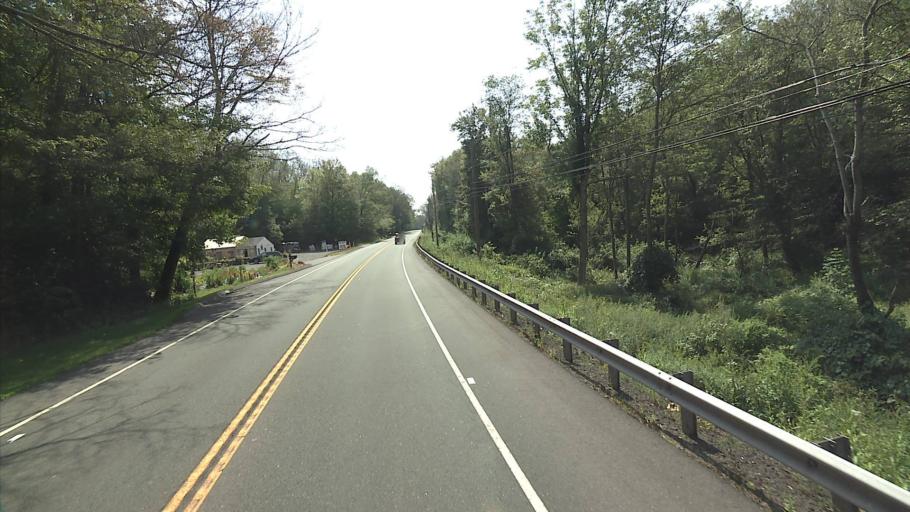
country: US
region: Connecticut
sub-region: Middlesex County
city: Durham
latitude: 41.4488
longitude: -72.6649
